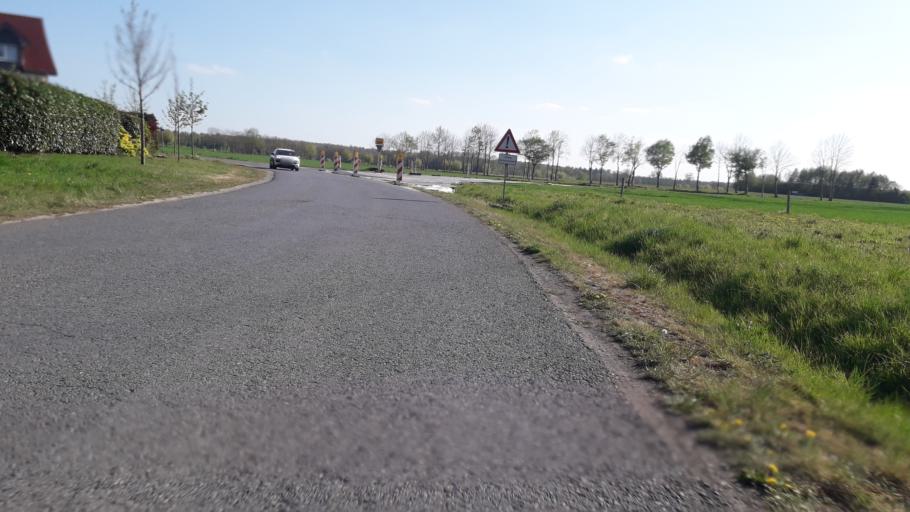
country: DE
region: North Rhine-Westphalia
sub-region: Regierungsbezirk Detmold
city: Salzkotten
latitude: 51.6920
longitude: 8.6785
